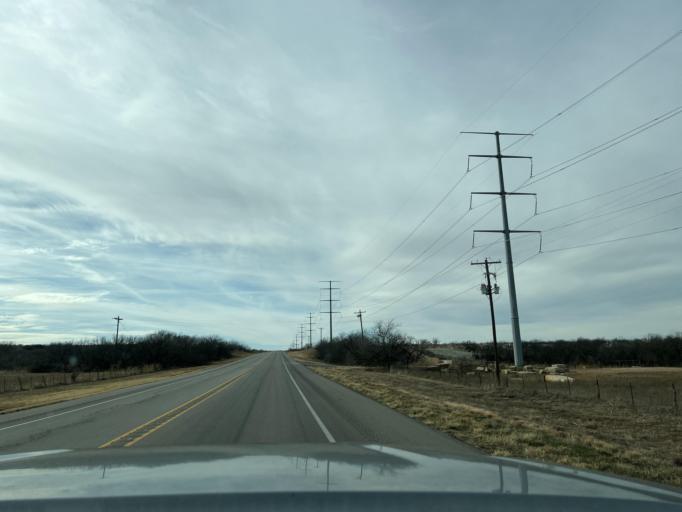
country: US
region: Texas
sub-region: Jones County
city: Stamford
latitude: 32.7503
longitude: -99.6333
